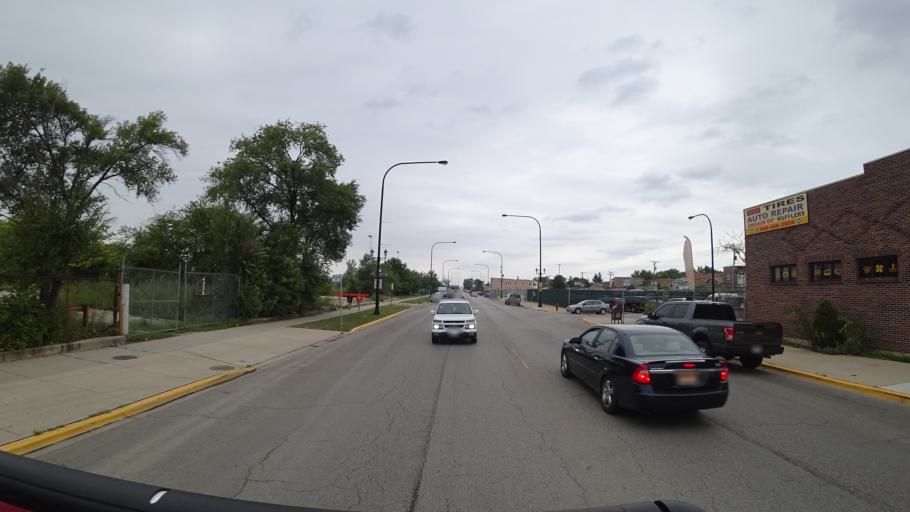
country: US
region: Illinois
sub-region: Cook County
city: Cicero
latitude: 41.8545
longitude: -87.7542
